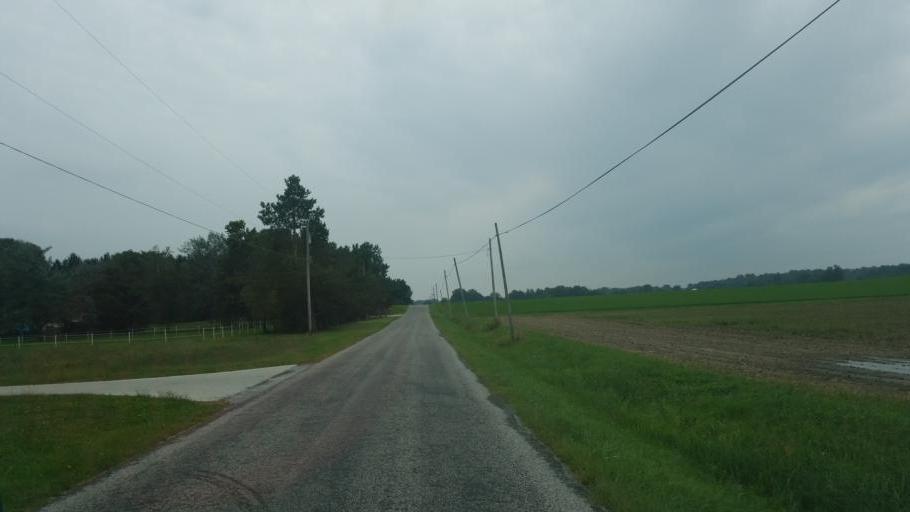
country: US
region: Ohio
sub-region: Wayne County
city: Creston
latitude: 40.9514
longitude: -81.8505
